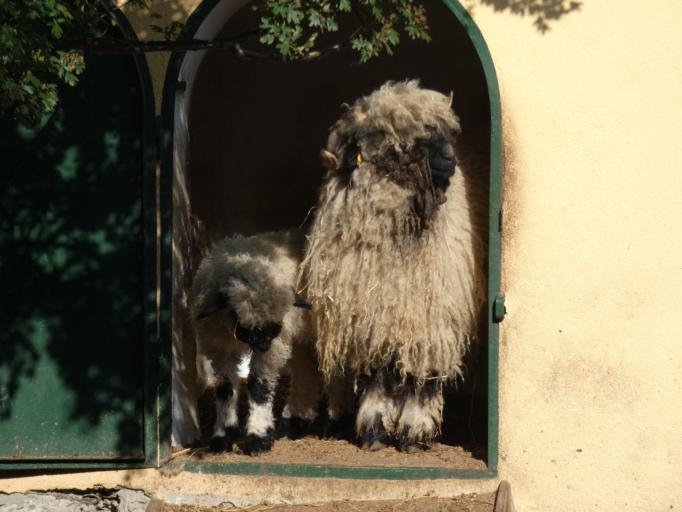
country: HU
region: Hajdu-Bihar
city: Debrecen
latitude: 47.5523
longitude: 21.6357
